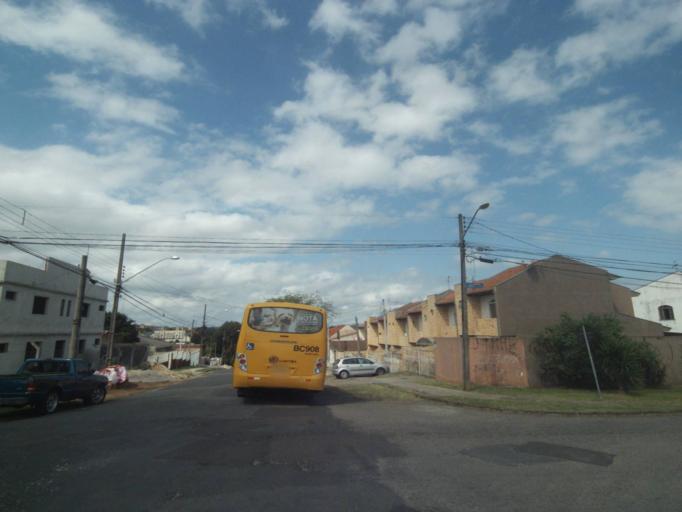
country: BR
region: Parana
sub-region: Pinhais
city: Pinhais
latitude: -25.4117
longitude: -49.2042
